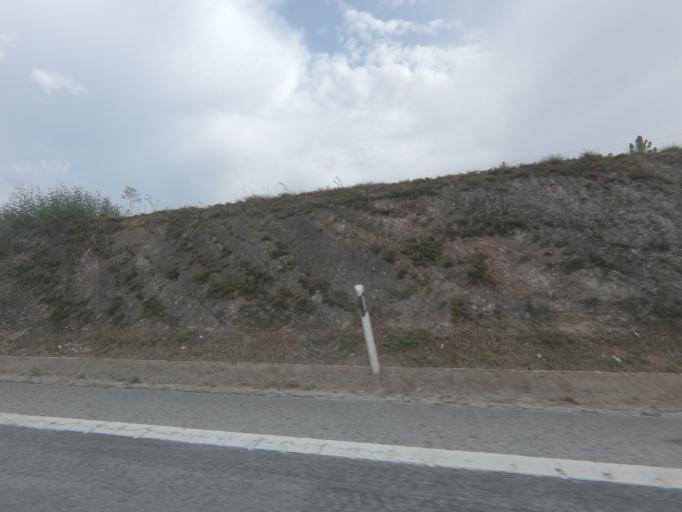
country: PT
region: Viseu
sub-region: Santa Comba Dao
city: Santa Comba Dao
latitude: 40.3501
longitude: -8.1630
